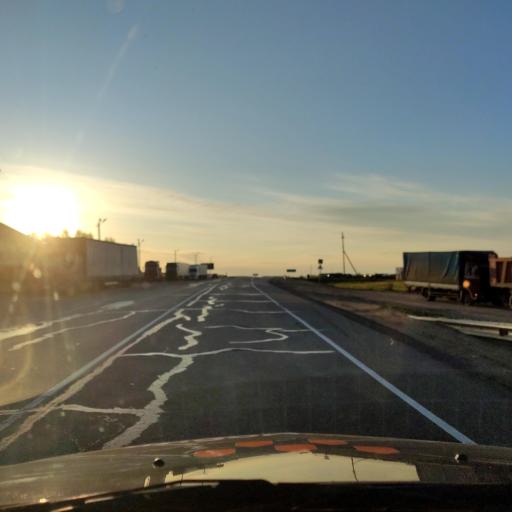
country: RU
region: Orjol
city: Livny
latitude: 52.4498
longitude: 37.5000
